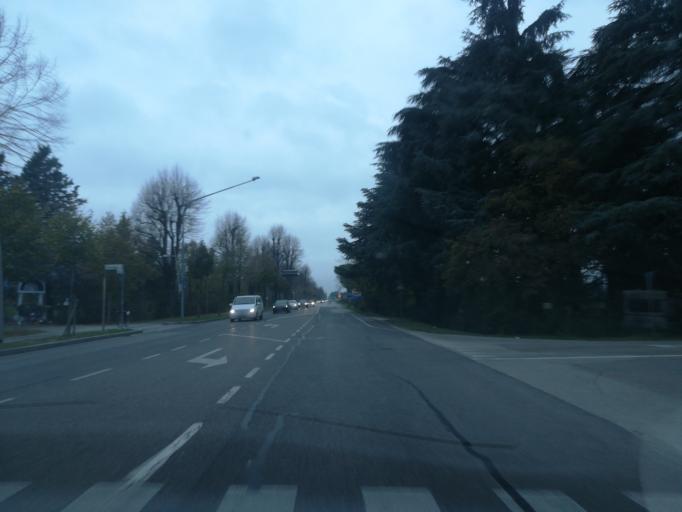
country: IT
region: Emilia-Romagna
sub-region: Provincia di Bologna
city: Imola
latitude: 44.3651
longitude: 11.6845
